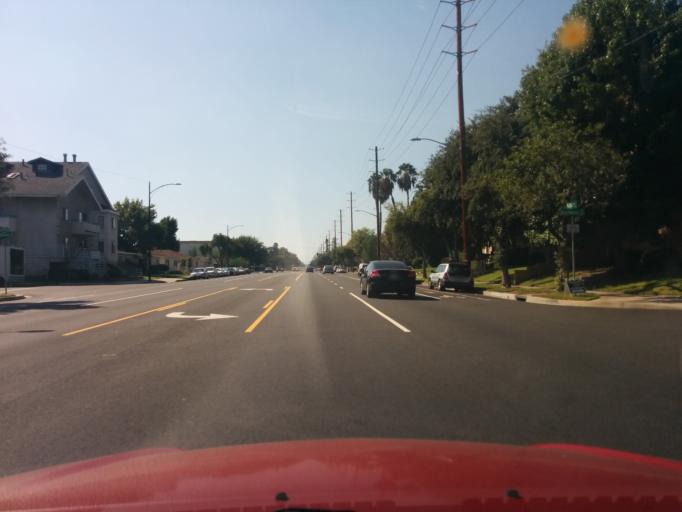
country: US
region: California
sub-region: Los Angeles County
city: Burbank
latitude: 34.1845
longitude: -118.3271
